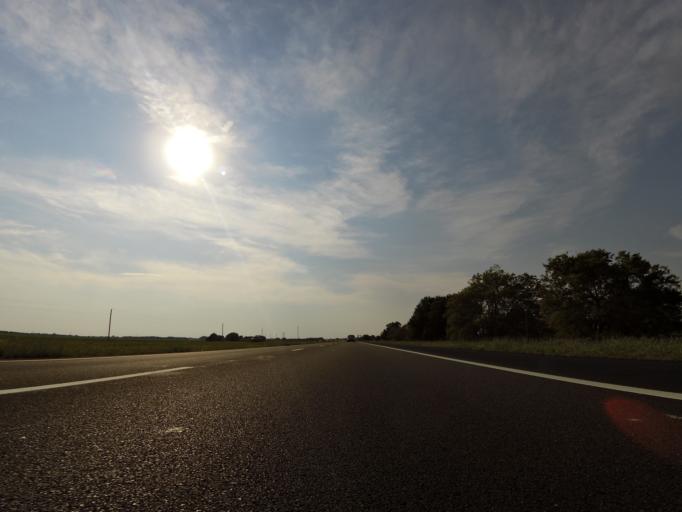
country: US
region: Kansas
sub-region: Reno County
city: Haven
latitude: 37.8902
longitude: -97.7506
